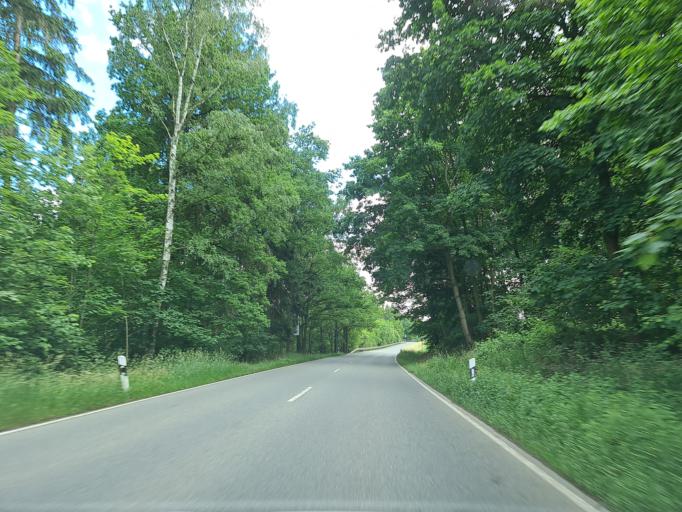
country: DE
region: Saxony
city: Pohl
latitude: 50.5438
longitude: 12.1817
